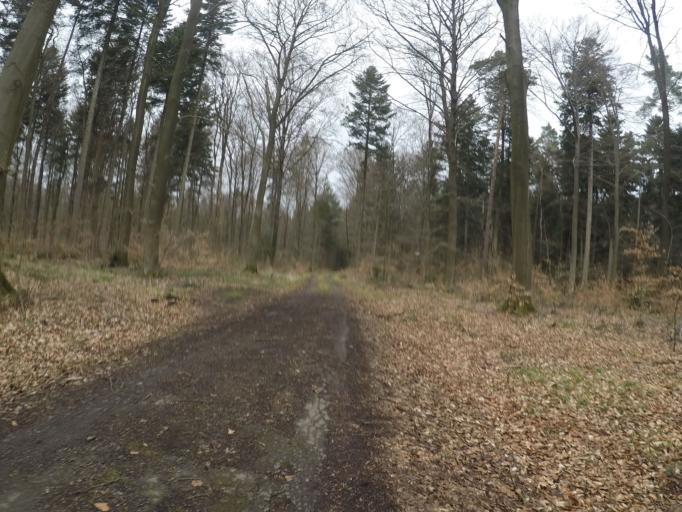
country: DE
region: Lower Saxony
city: Drangstedt
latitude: 53.6184
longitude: 8.7195
